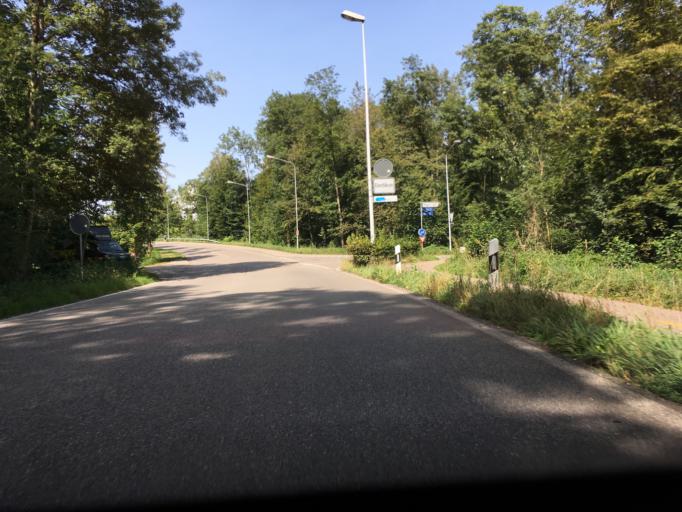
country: CH
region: Zurich
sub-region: Bezirk Buelach
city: Dietlikon / Dietlikon (Dorf)
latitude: 47.4104
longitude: 8.6225
